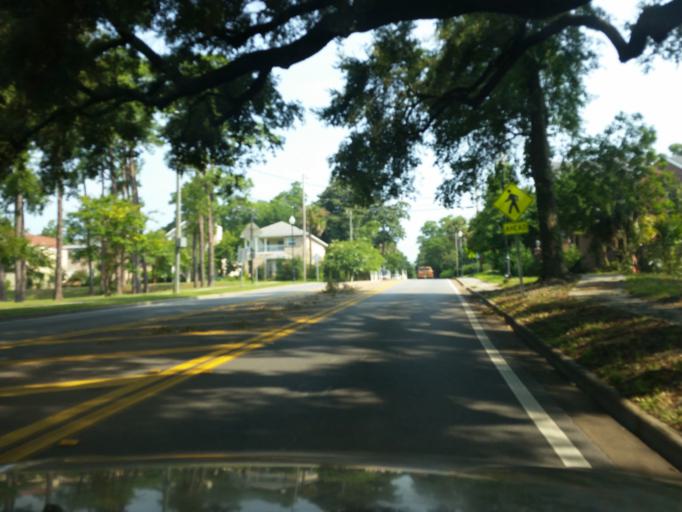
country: US
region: Florida
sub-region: Escambia County
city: East Pensacola Heights
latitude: 30.4215
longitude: -87.1944
